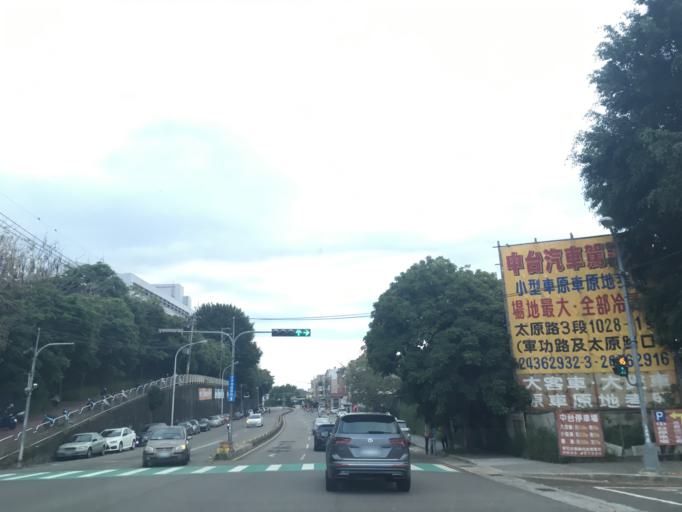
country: TW
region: Taiwan
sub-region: Taichung City
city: Taichung
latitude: 24.1753
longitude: 120.7356
